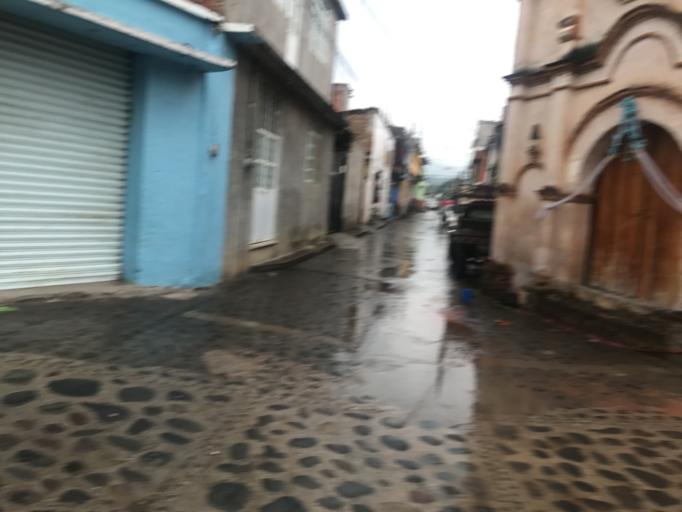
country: MX
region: Morelos
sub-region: Tlayacapan
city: Tlayacapan
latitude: 18.9561
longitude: -98.9856
